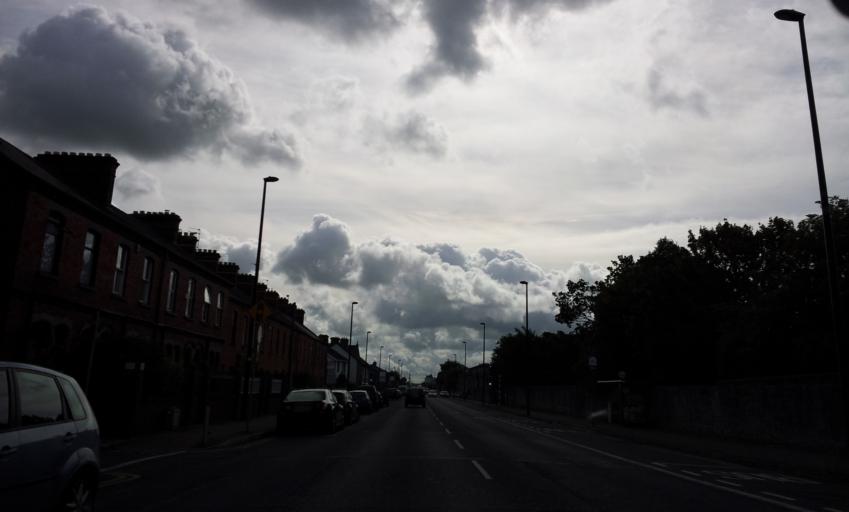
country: IE
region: Munster
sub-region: County Limerick
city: Luimneach
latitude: 52.6589
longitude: -8.6148
